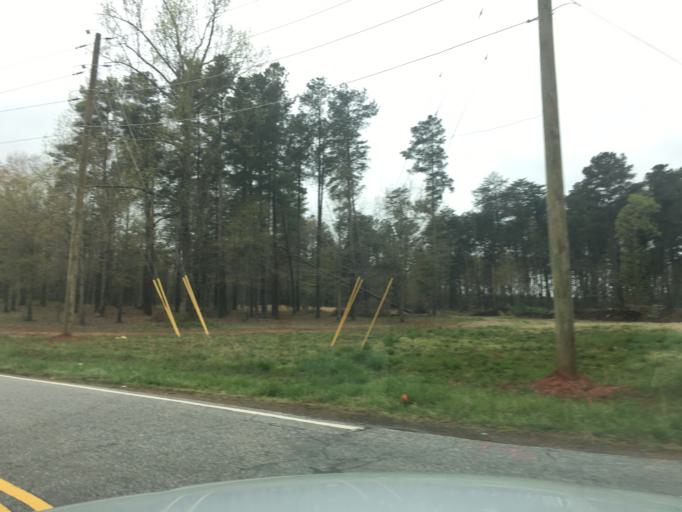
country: US
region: South Carolina
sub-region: Spartanburg County
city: Fairforest
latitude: 34.9708
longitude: -82.0501
